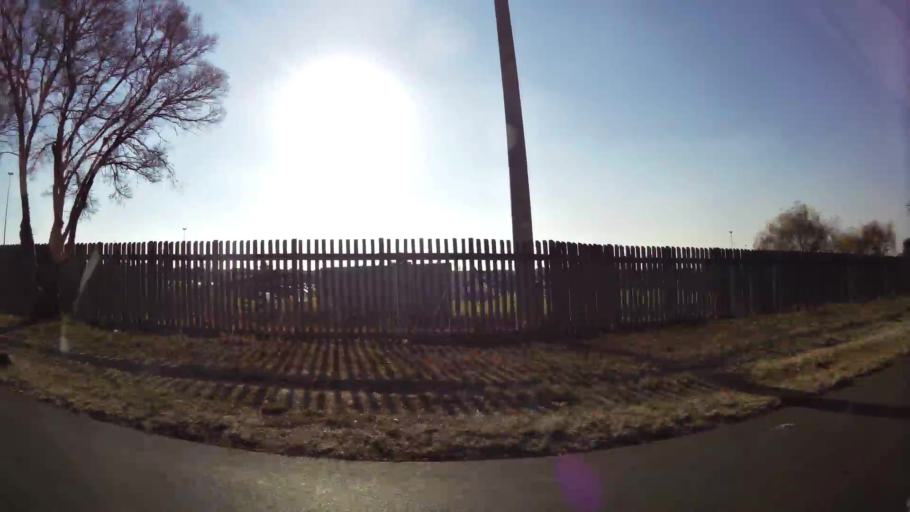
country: ZA
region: Gauteng
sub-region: City of Johannesburg Metropolitan Municipality
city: Soweto
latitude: -26.2662
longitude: 27.8677
